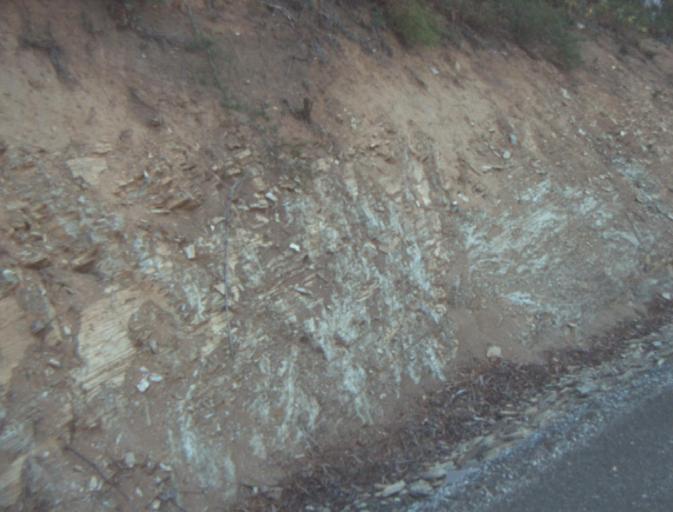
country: AU
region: Tasmania
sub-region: Dorset
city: Scottsdale
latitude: -41.2938
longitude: 147.3407
